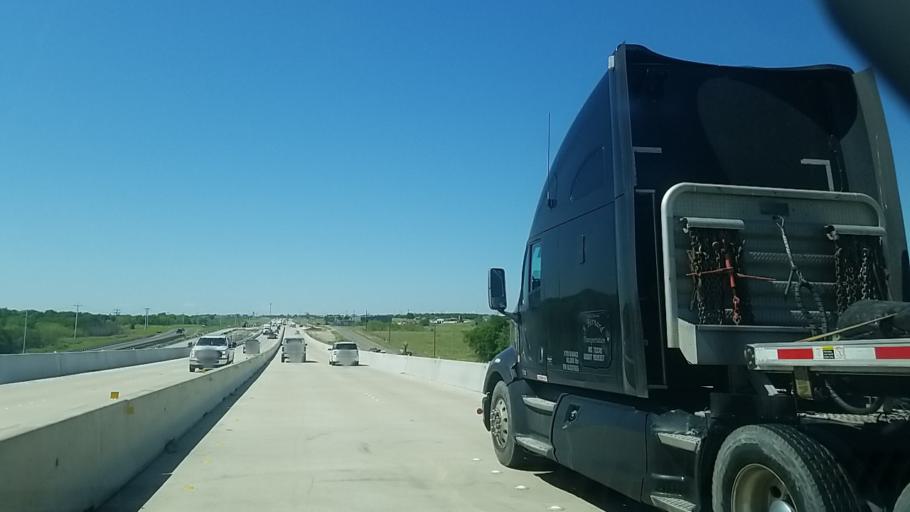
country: US
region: Texas
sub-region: Navarro County
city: Corsicana
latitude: 32.0439
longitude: -96.4474
